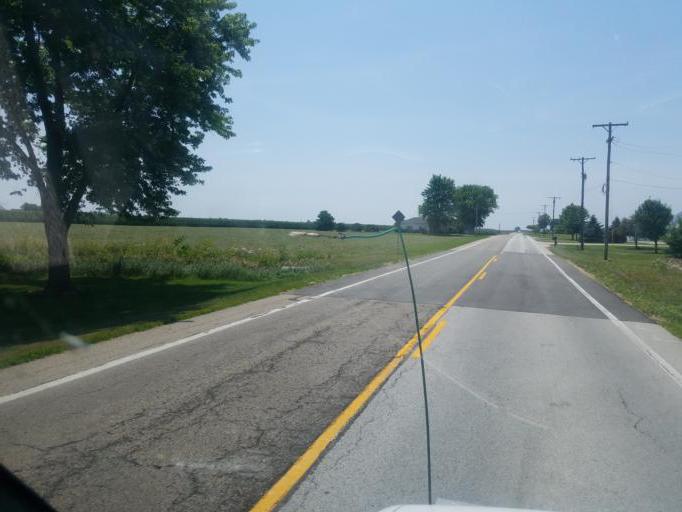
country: US
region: Ohio
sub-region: Shelby County
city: Fort Loramie
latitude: 40.3417
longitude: -84.4208
